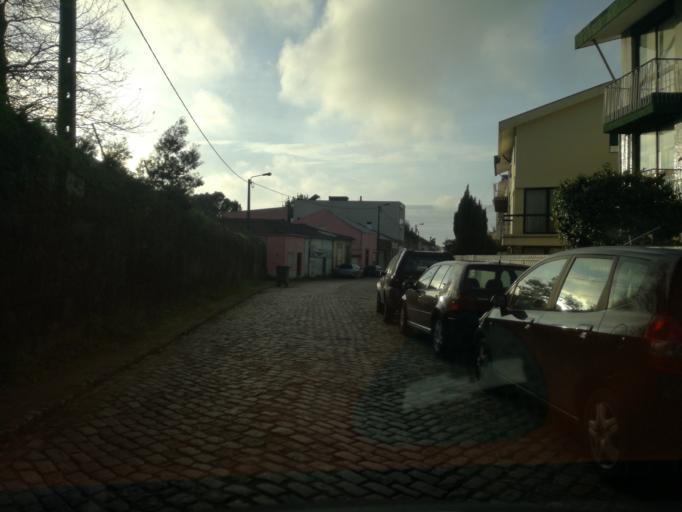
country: PT
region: Porto
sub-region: Matosinhos
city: Senhora da Hora
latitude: 41.1754
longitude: -8.6320
